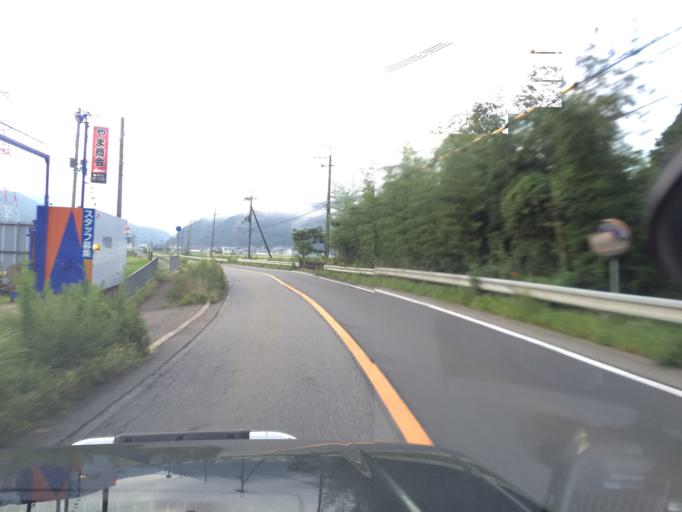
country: JP
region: Hyogo
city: Nishiwaki
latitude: 35.1134
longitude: 135.0008
